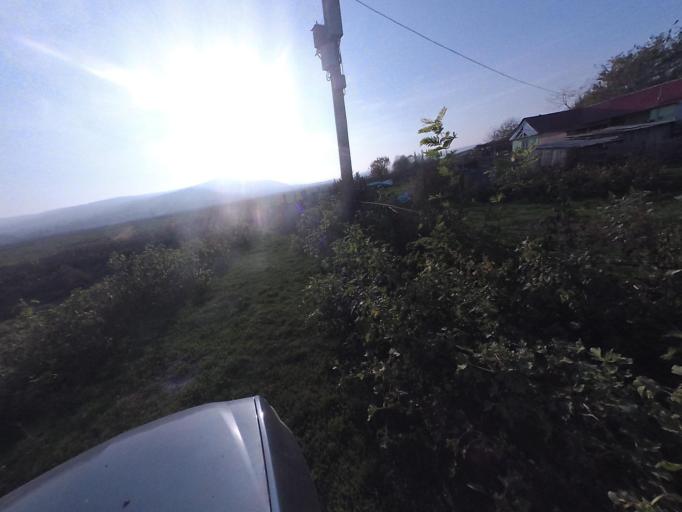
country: RO
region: Vaslui
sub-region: Comuna Bacesti
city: Bacesti
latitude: 46.8174
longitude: 27.2310
